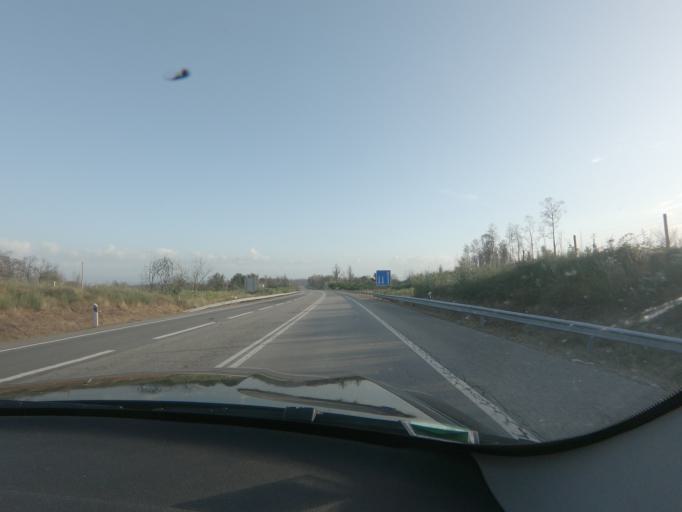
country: PT
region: Viseu
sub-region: Concelho de Tondela
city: Tondela
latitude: 40.4650
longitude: -8.1002
